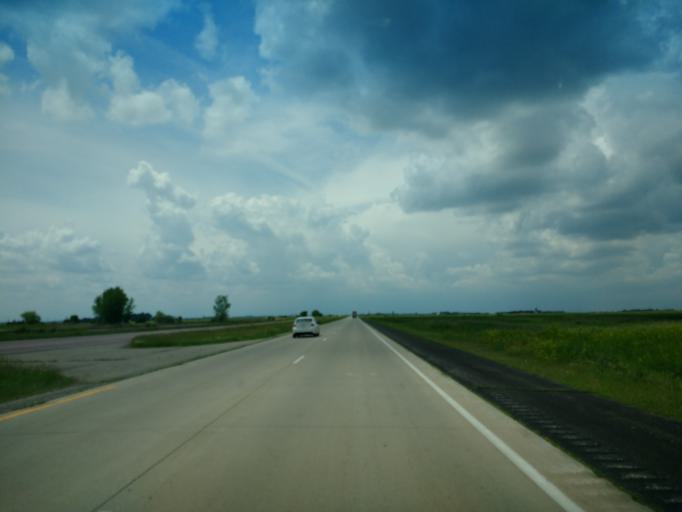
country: US
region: Minnesota
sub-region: Cottonwood County
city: Windom
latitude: 43.8222
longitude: -95.2246
